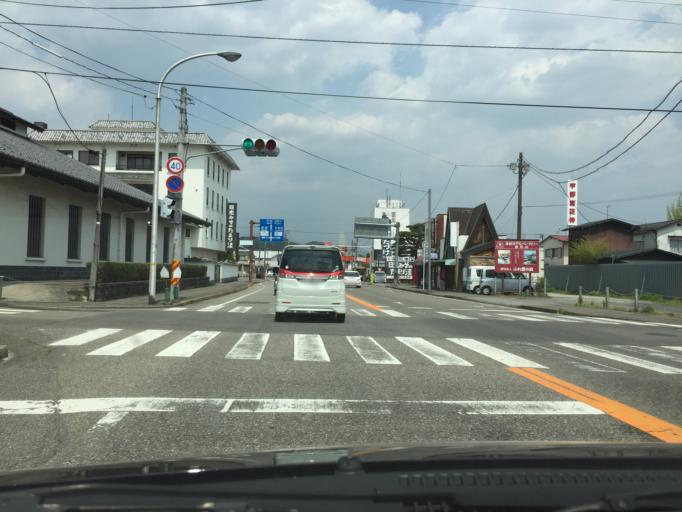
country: JP
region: Tochigi
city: Imaichi
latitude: 36.7241
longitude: 139.6841
